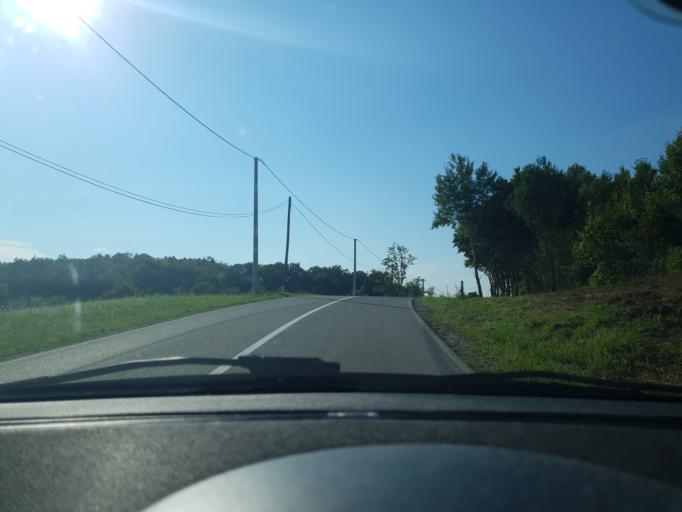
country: HR
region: Zagrebacka
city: Jablanovec
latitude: 45.9130
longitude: 15.8470
